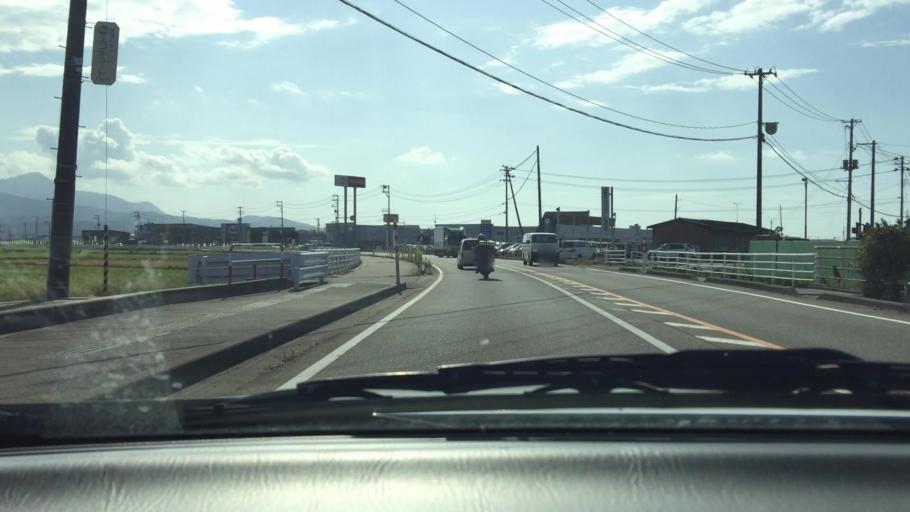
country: JP
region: Niigata
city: Kashiwazaki
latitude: 37.3877
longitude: 138.5871
